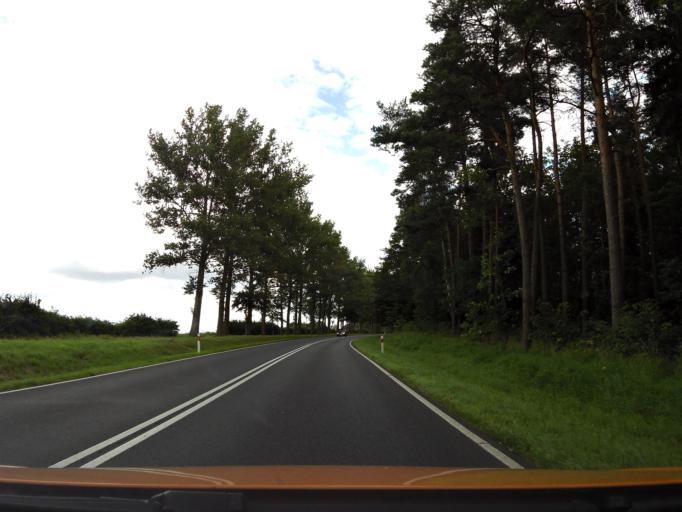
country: PL
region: West Pomeranian Voivodeship
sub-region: Powiat gryficki
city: Ploty
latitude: 53.8296
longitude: 15.2908
